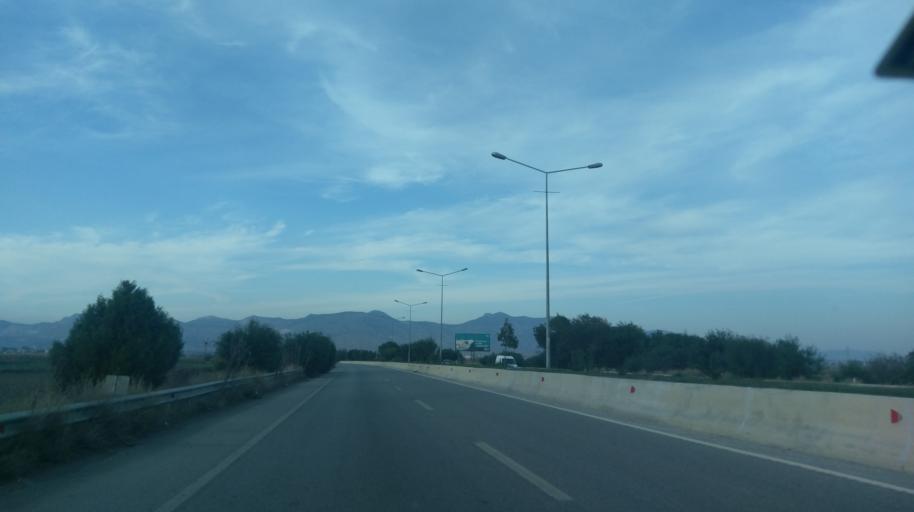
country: CY
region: Lefkosia
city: Geri
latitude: 35.1862
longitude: 33.5028
